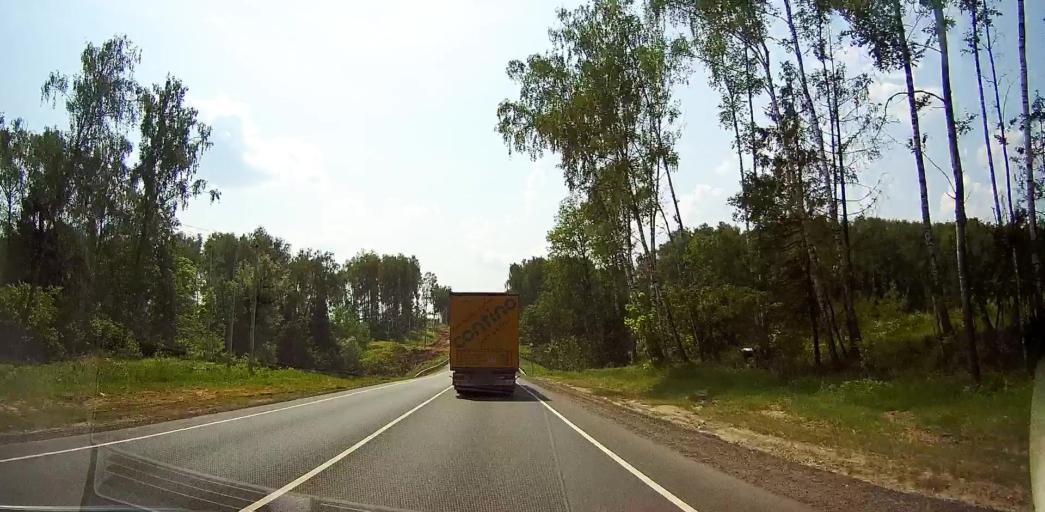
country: RU
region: Moskovskaya
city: Meshcherino
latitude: 55.2030
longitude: 38.3766
